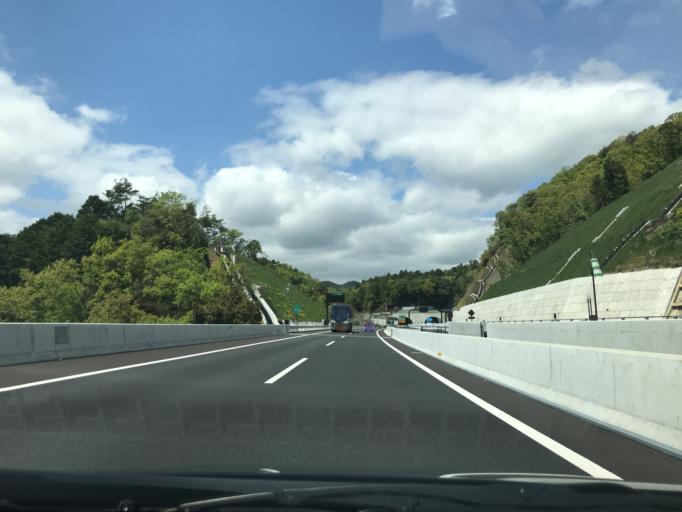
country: JP
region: Osaka
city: Takatsuki
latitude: 34.8910
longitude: 135.6101
